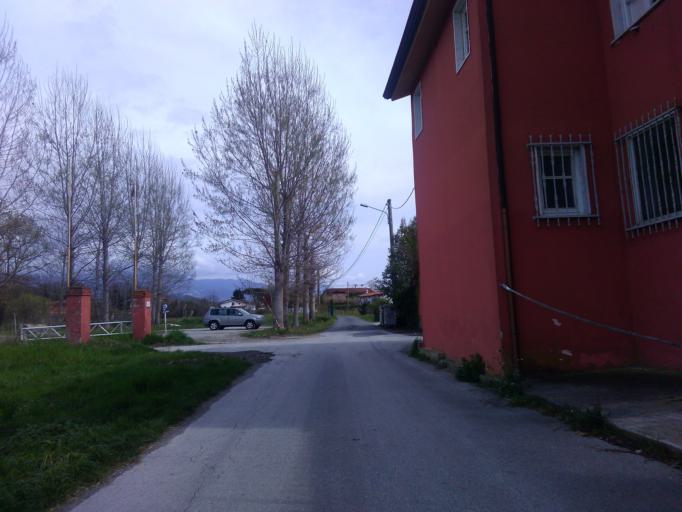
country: IT
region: Liguria
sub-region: Provincia di La Spezia
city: Casano-Dogana-Isola
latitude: 44.0560
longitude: 10.0286
